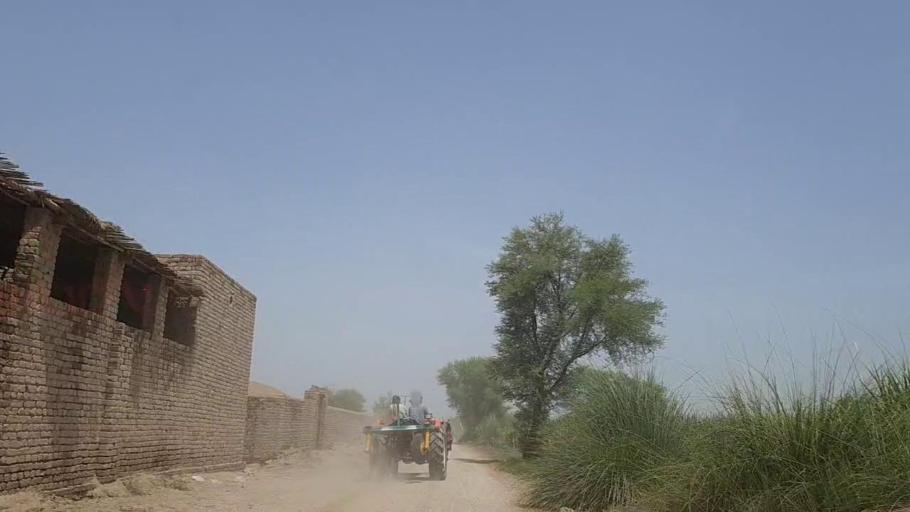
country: PK
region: Sindh
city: Tharu Shah
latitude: 26.8963
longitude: 68.0092
